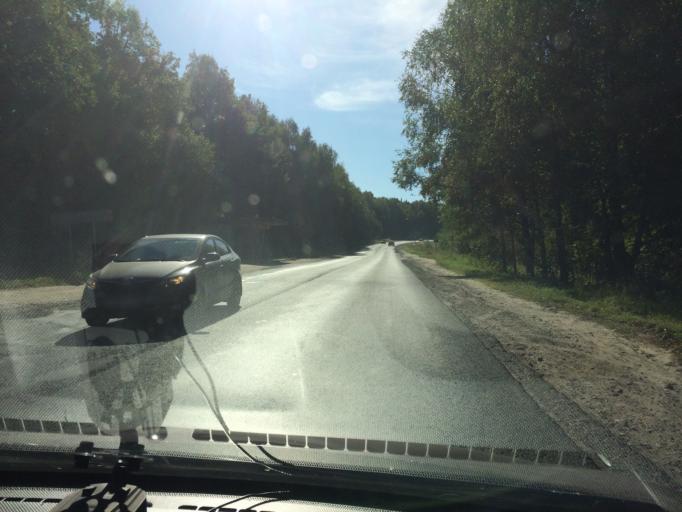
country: RU
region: Mariy-El
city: Yoshkar-Ola
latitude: 56.6087
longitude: 47.9665
